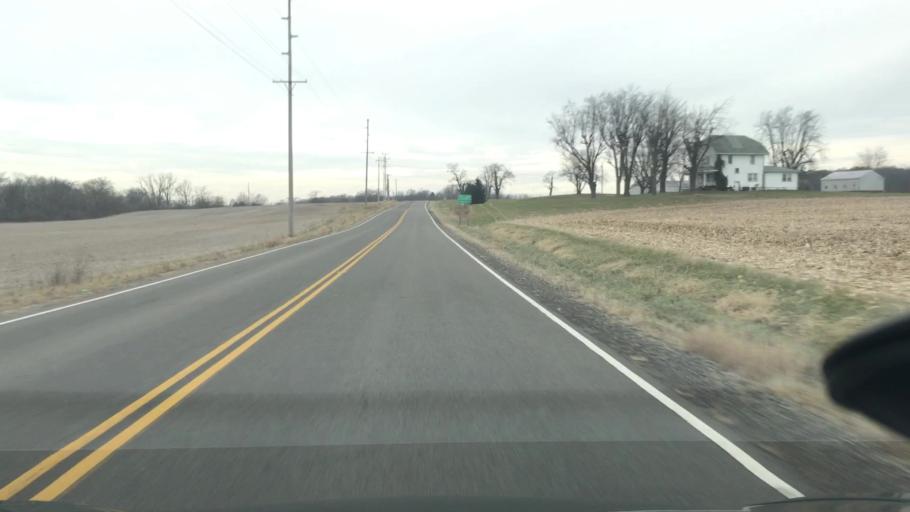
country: US
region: Ohio
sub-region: Madison County
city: London
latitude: 39.8596
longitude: -83.4094
